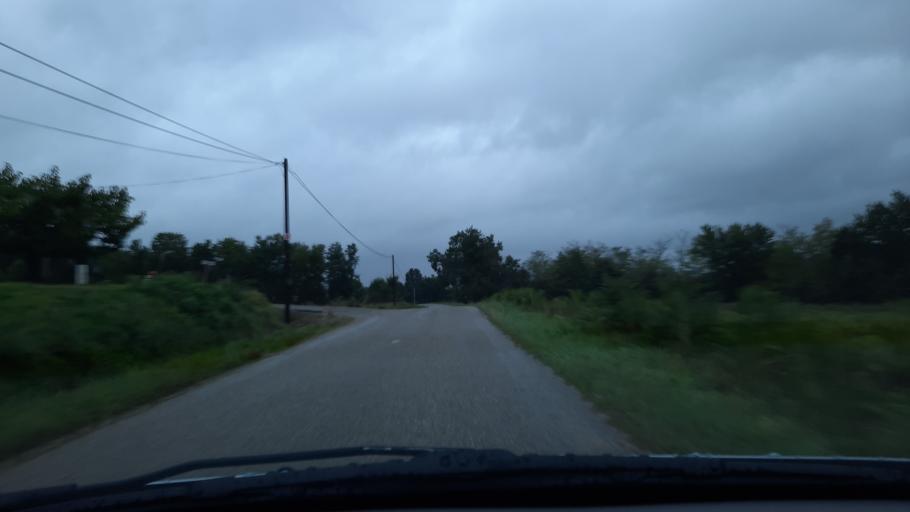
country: FR
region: Midi-Pyrenees
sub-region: Departement du Tarn-et-Garonne
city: Lafrancaise
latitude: 44.1865
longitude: 1.2761
